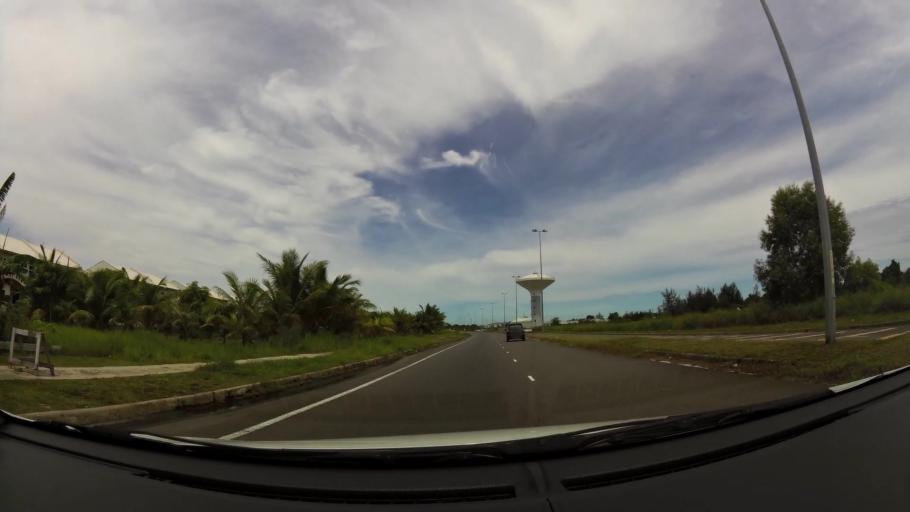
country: BN
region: Belait
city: Kuala Belait
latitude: 4.5895
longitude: 114.2645
